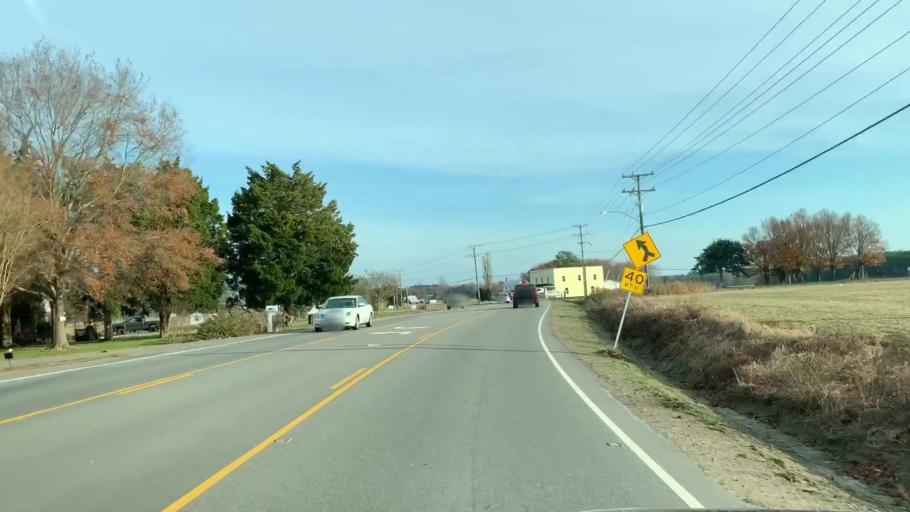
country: US
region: Virginia
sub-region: City of Virginia Beach
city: Virginia Beach
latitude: 36.6930
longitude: -76.0250
